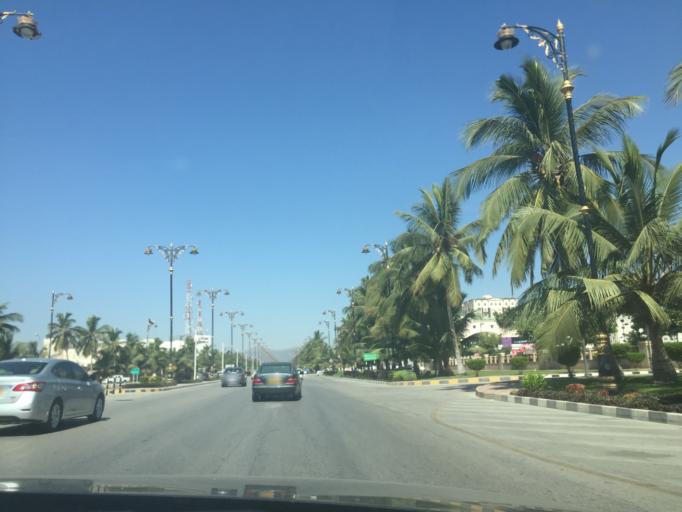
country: OM
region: Zufar
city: Salalah
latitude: 17.0164
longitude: 54.0929
